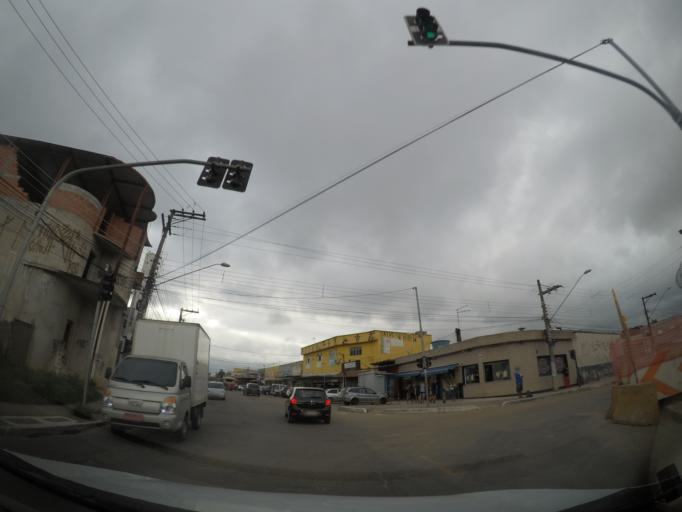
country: BR
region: Sao Paulo
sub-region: Aruja
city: Aruja
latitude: -23.3977
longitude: -46.4292
